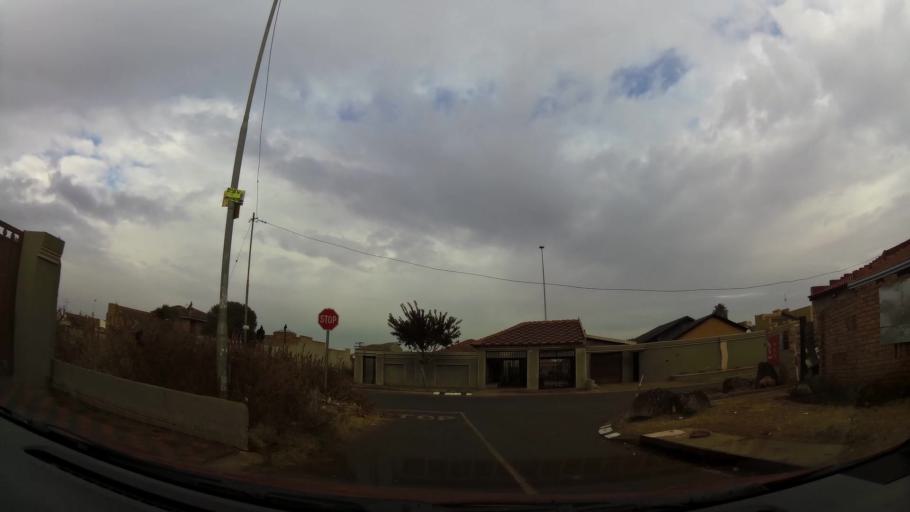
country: ZA
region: Gauteng
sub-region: City of Johannesburg Metropolitan Municipality
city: Soweto
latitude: -26.2825
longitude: 27.8372
